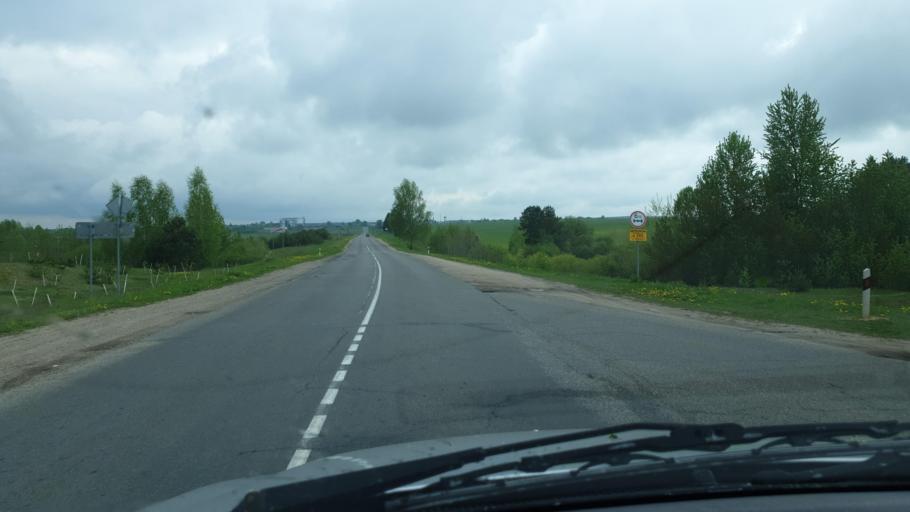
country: BY
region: Vitebsk
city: Lyepyel'
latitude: 54.8827
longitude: 28.6546
